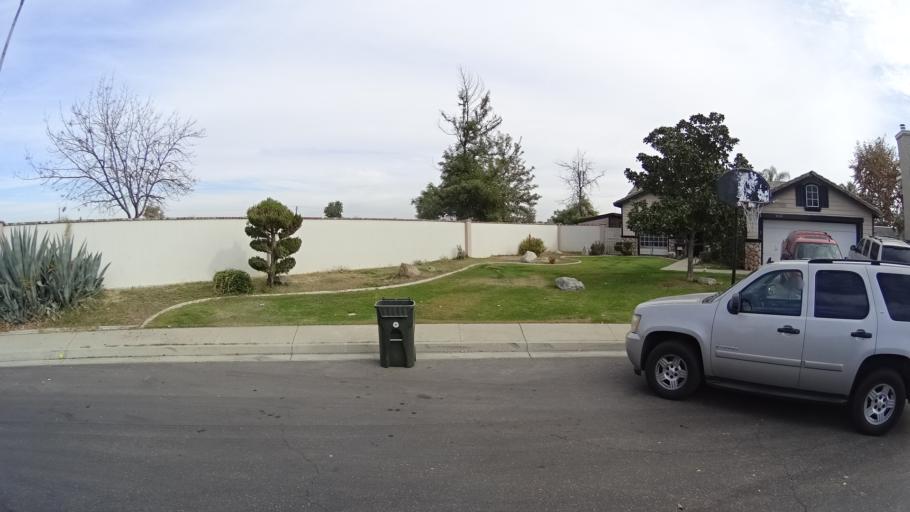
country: US
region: California
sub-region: Kern County
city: Rosedale
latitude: 35.4032
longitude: -119.1318
